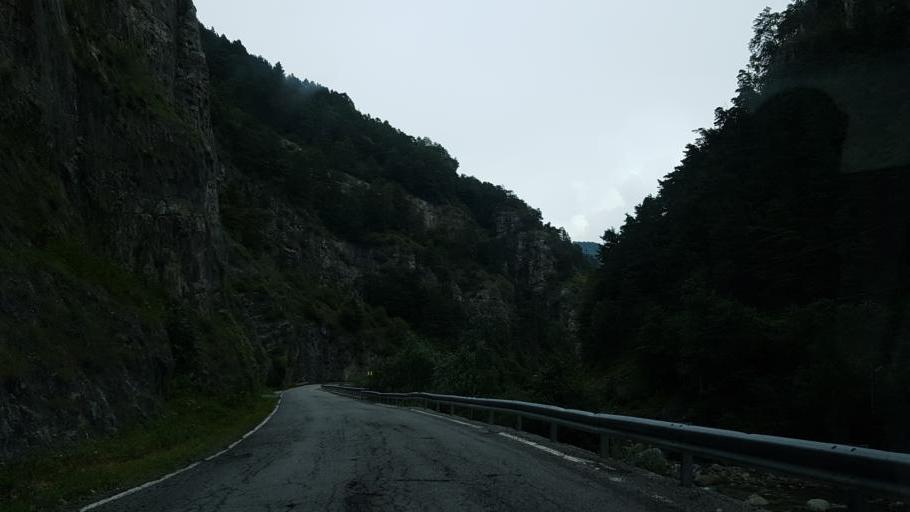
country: IT
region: Piedmont
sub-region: Provincia di Cuneo
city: Stroppo
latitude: 44.4954
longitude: 7.1033
